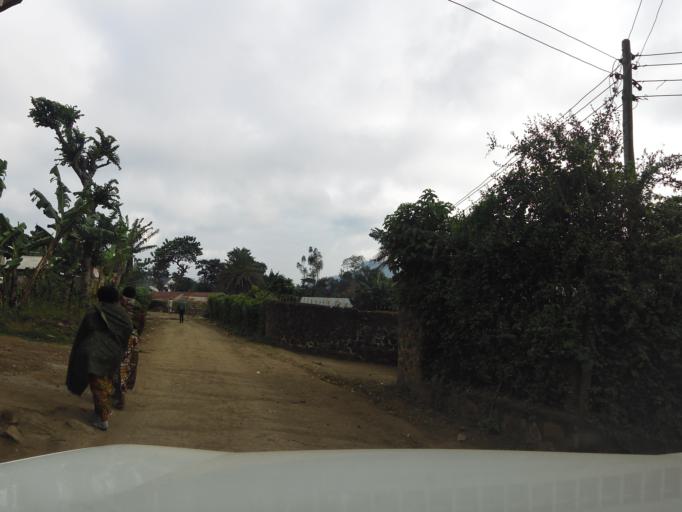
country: TZ
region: Arusha
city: Arusha
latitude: -3.3739
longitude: 36.7171
